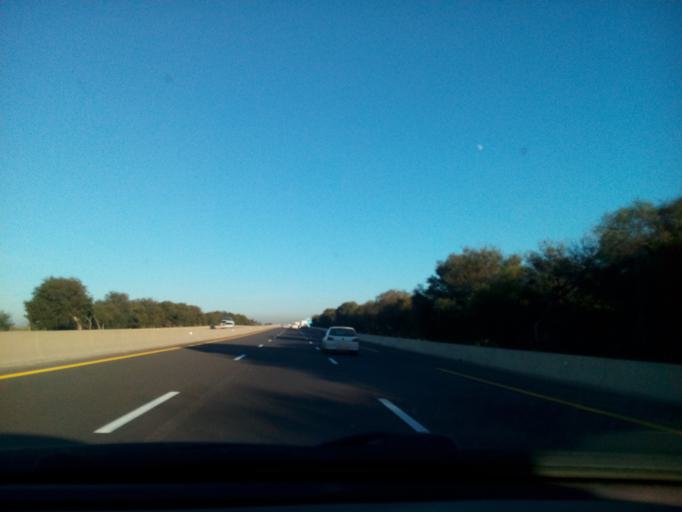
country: DZ
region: Relizane
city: Djidiouia
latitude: 35.9153
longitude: 0.7520
